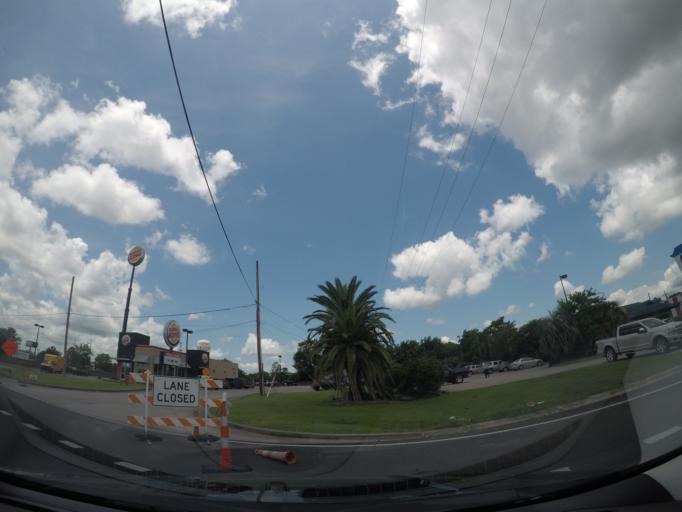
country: US
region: Louisiana
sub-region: Calcasieu Parish
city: Sulphur
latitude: 30.2192
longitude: -93.3763
